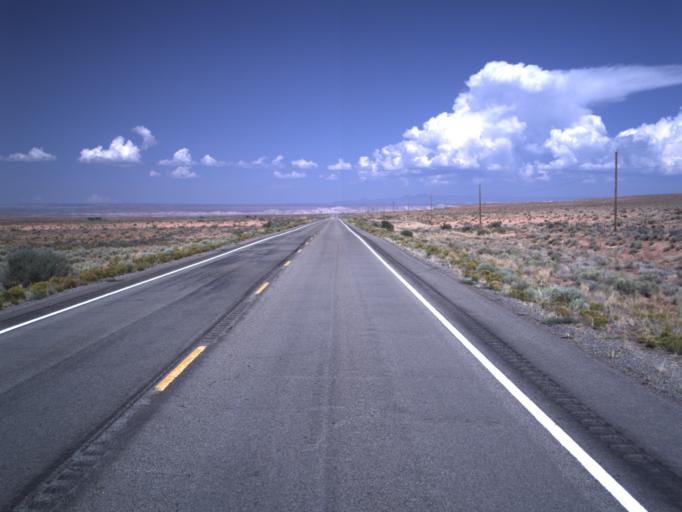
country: US
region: Utah
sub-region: San Juan County
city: Blanding
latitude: 37.1306
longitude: -109.5507
